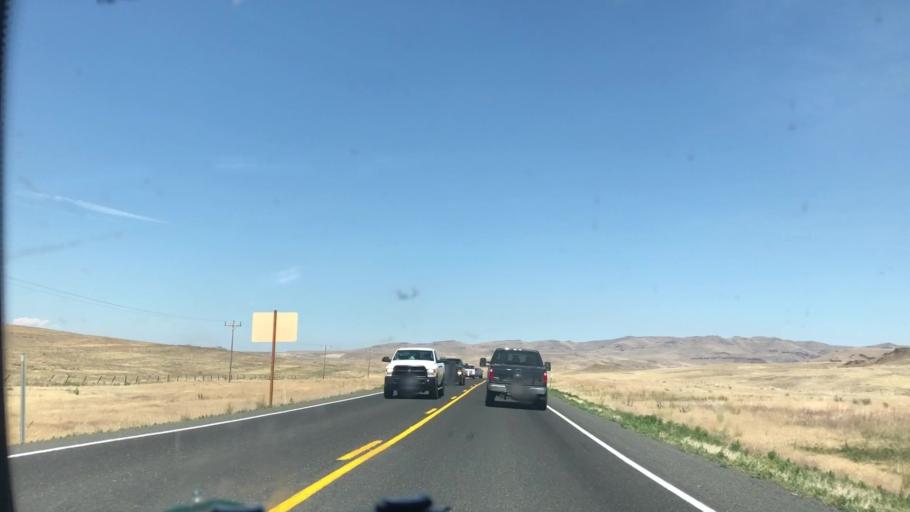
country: US
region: Idaho
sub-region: Owyhee County
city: Marsing
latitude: 43.2462
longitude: -117.0338
